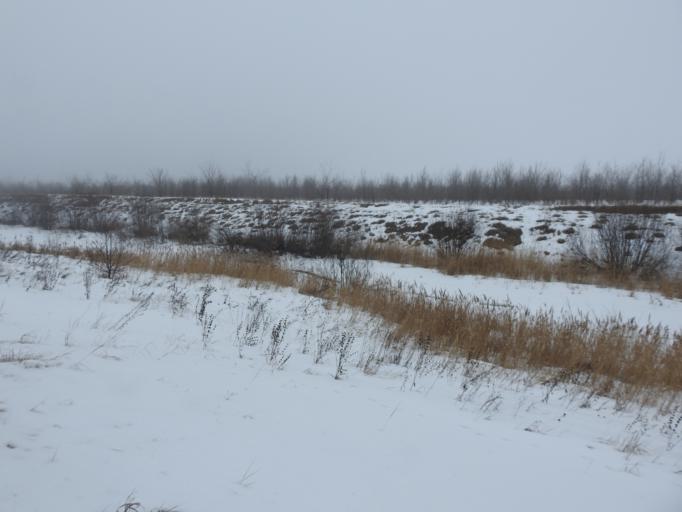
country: RU
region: Saratov
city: Sokolovyy
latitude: 51.4980
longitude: 45.8236
